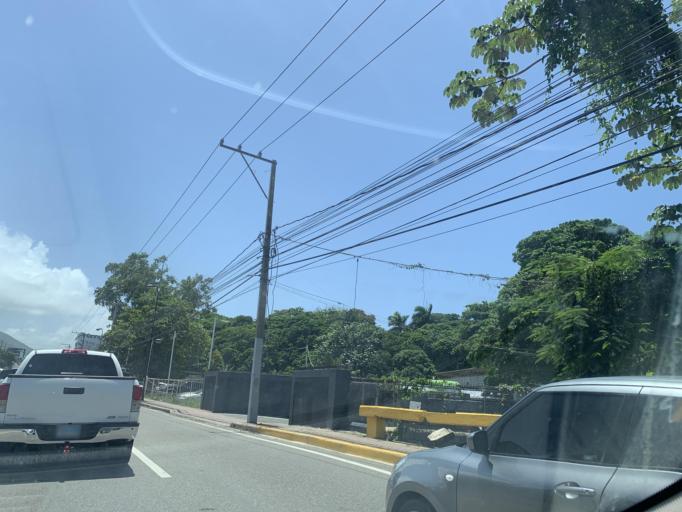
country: DO
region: Puerto Plata
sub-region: Puerto Plata
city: Puerto Plata
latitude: 19.7771
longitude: -70.6617
